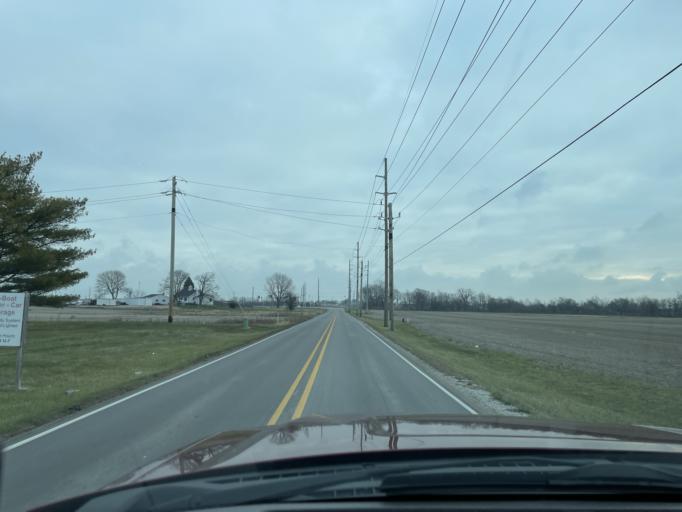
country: US
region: Indiana
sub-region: Boone County
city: Whitestown
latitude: 39.9459
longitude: -86.3638
